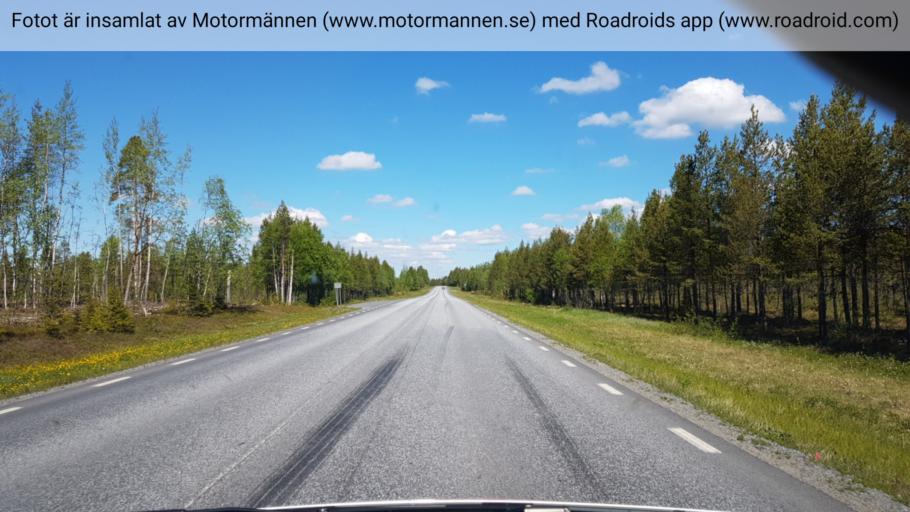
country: SE
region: Vaesterbotten
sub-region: Vilhelmina Kommun
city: Vilhelmina
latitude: 64.5901
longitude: 16.7370
